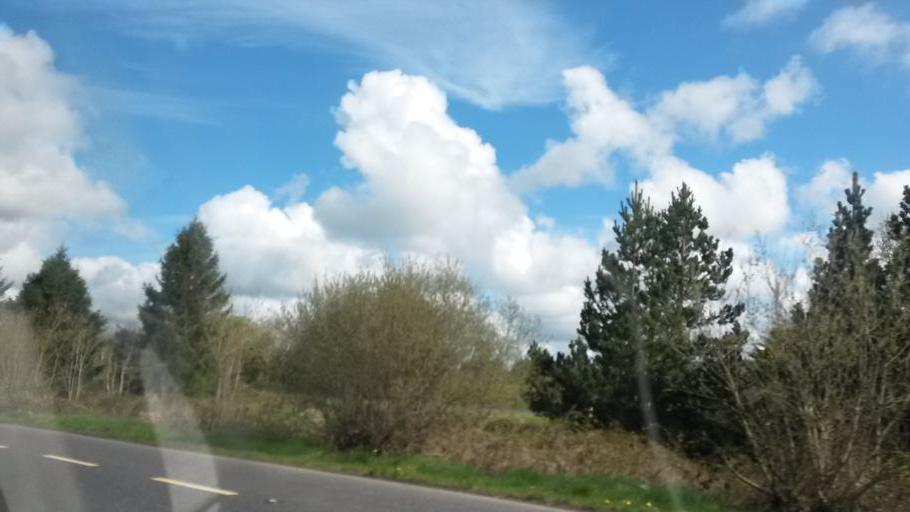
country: IE
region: Ulster
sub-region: An Cabhan
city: Ballyjamesduff
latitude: 53.8898
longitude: -7.1542
